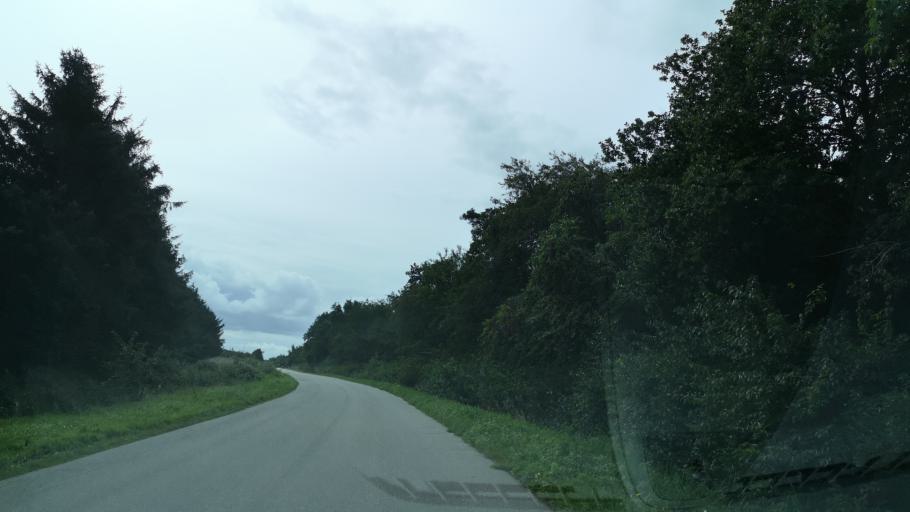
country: DK
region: South Denmark
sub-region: Varde Kommune
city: Oksbol
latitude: 55.8341
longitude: 8.2811
